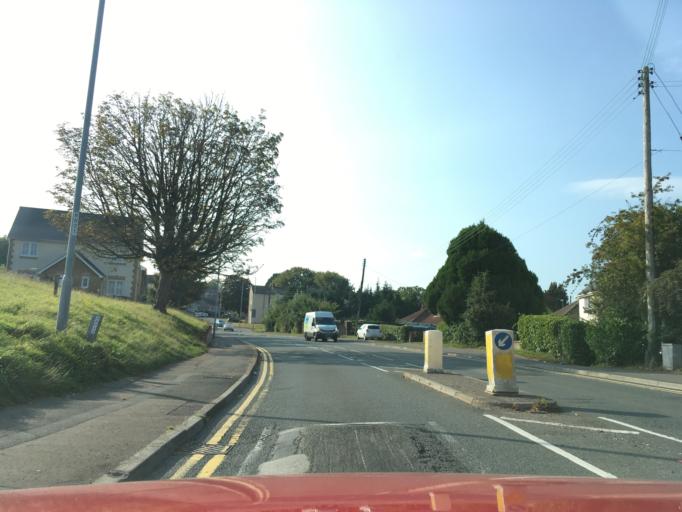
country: GB
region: Wales
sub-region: Newport
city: Newport
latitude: 51.6082
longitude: -3.0170
